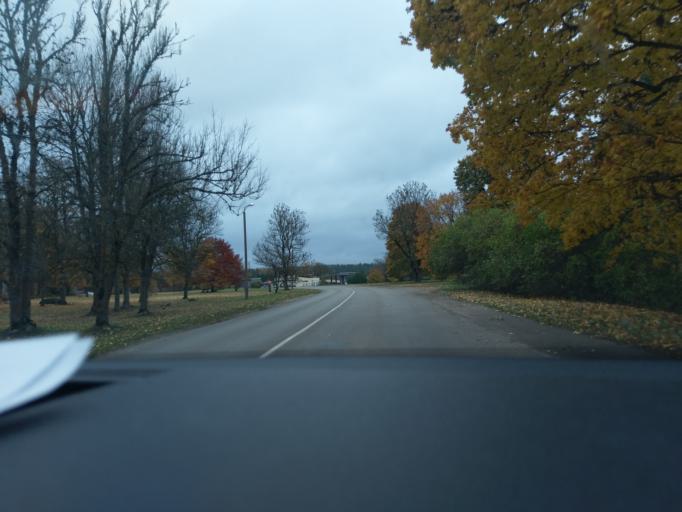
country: LV
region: Talsu Rajons
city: Stende
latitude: 57.0667
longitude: 22.2925
